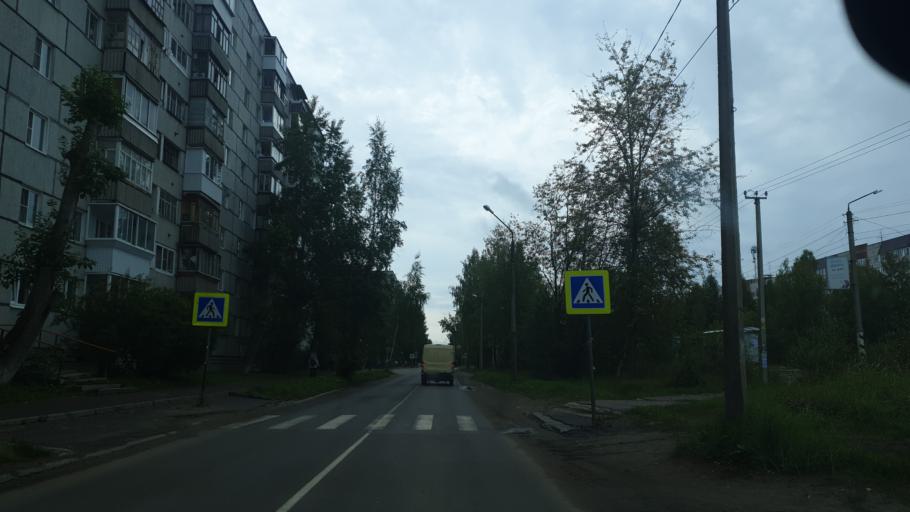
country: RU
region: Komi Republic
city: Ezhva
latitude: 61.7900
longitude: 50.7428
